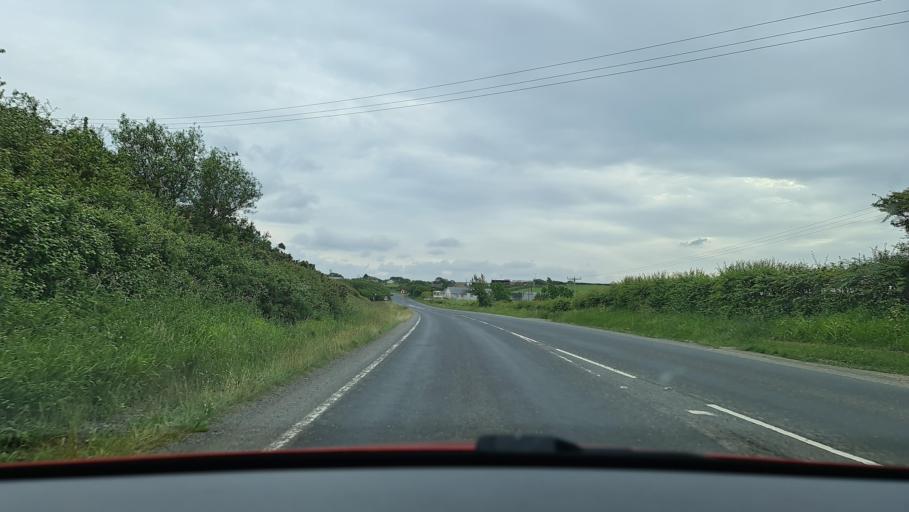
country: GB
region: England
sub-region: Cornwall
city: Poundstock
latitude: 50.7767
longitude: -4.5415
